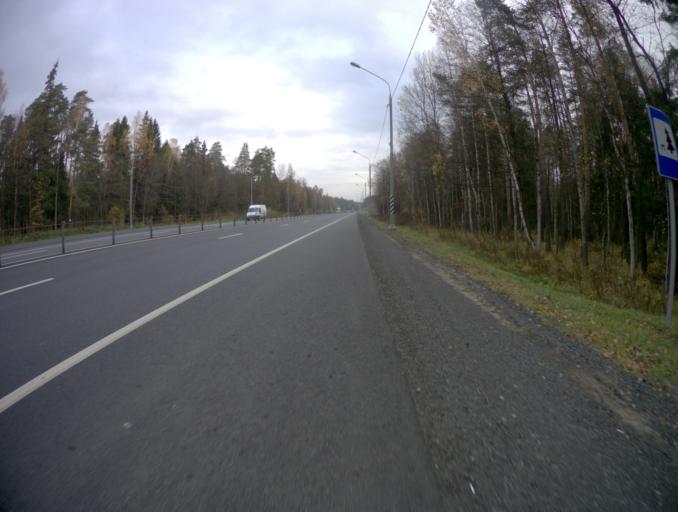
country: RU
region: Moskovskaya
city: Malaya Dubna
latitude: 55.8574
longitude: 38.9625
